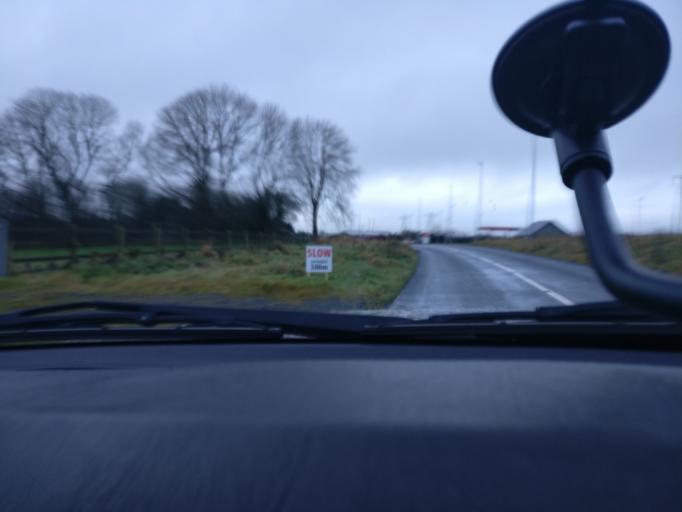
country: IE
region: Connaught
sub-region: County Galway
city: Loughrea
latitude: 53.2645
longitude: -8.6009
